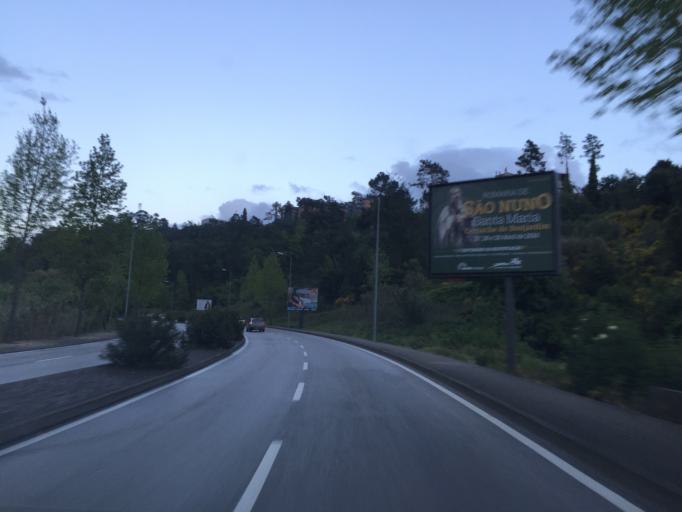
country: PT
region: Coimbra
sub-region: Coimbra
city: Coimbra
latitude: 40.2186
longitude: -8.4278
